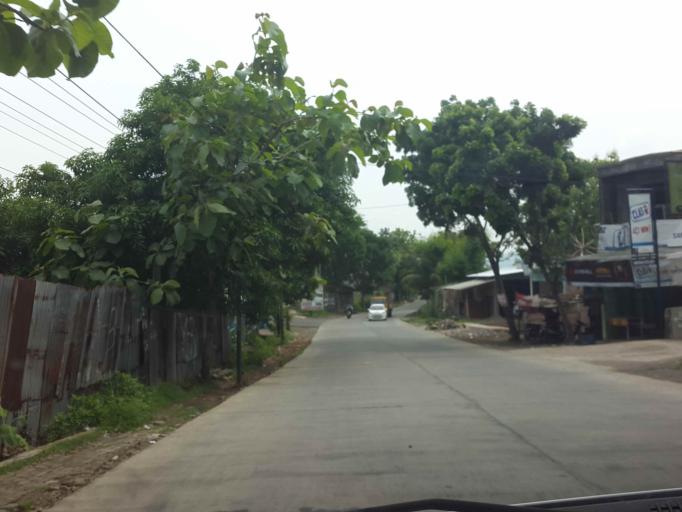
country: ID
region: Central Java
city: Mranggen
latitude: -7.0463
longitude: 110.4630
